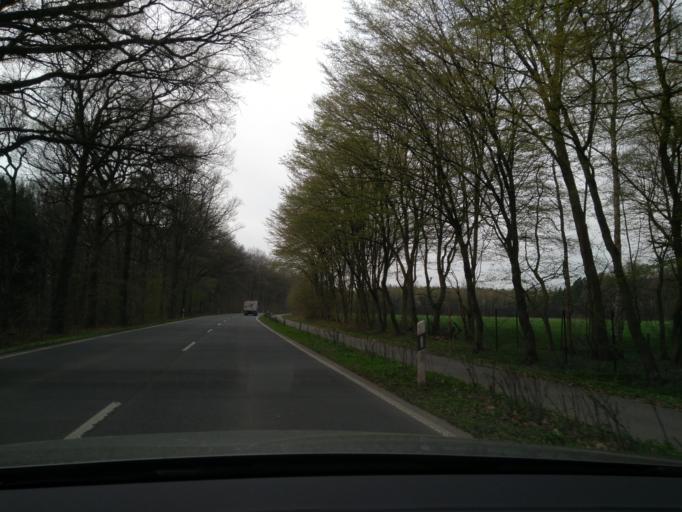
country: DE
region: North Rhine-Westphalia
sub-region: Regierungsbezirk Dusseldorf
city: Issum
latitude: 51.5797
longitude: 6.4496
